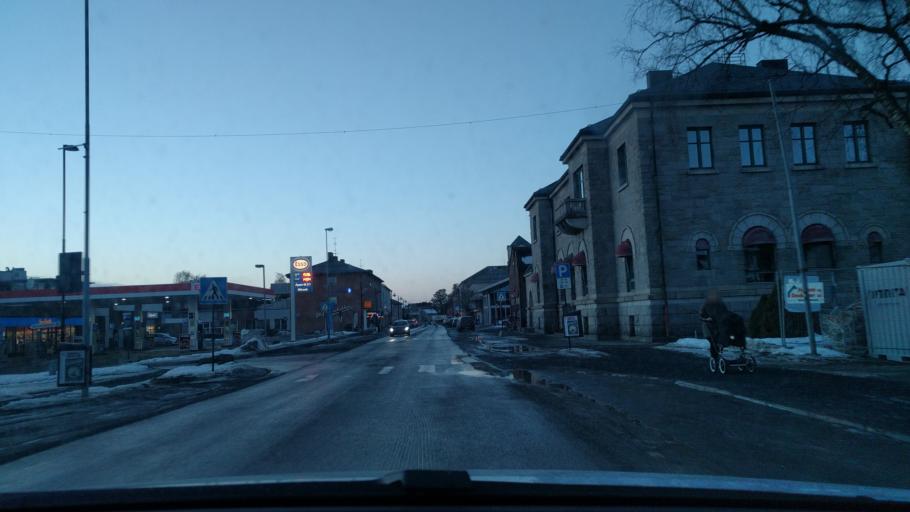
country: NO
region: Hedmark
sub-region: Elverum
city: Elverum
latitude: 60.8796
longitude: 11.5644
